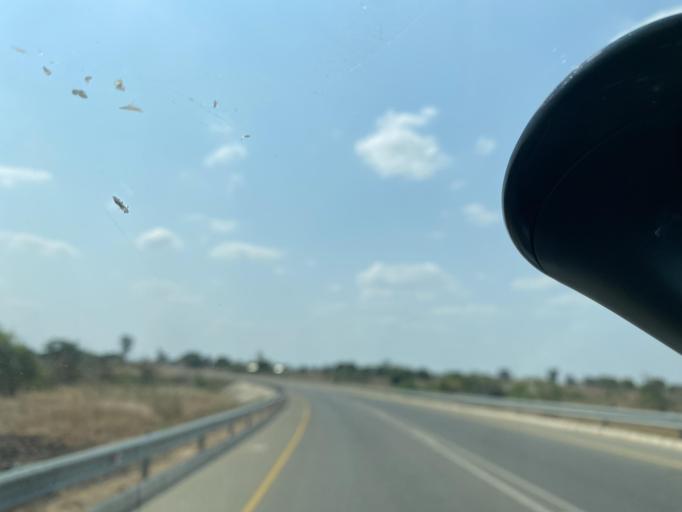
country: ZM
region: Lusaka
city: Chongwe
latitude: -15.5802
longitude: 28.7053
